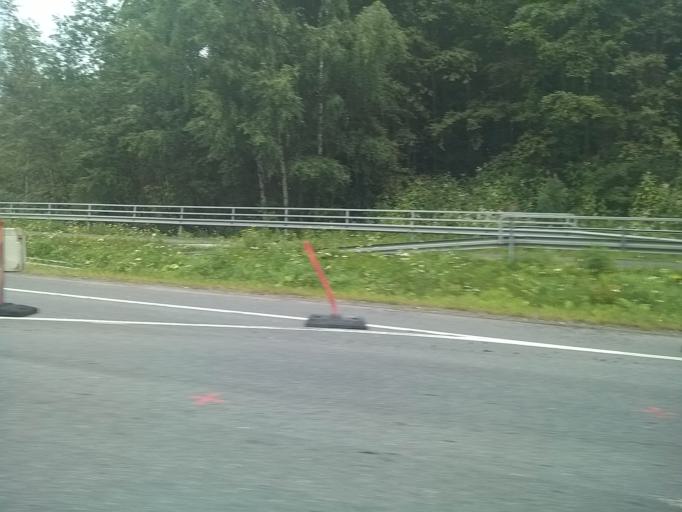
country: FI
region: Pirkanmaa
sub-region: Tampere
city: Tampere
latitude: 61.4891
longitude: 23.8244
